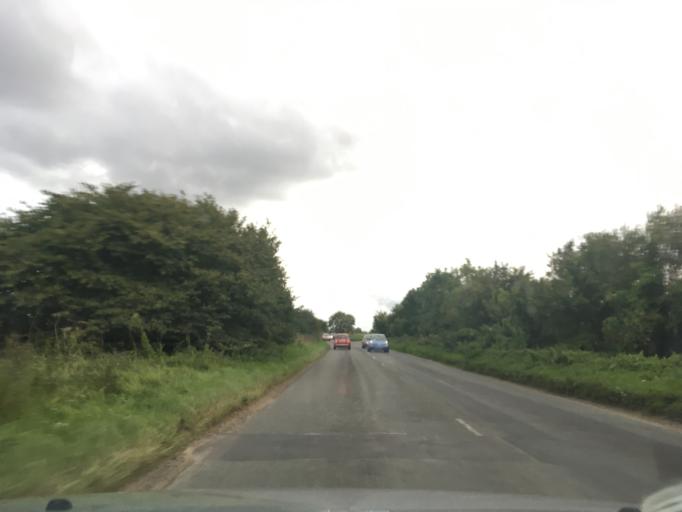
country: GB
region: England
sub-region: Oxfordshire
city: Wheatley
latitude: 51.7826
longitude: -1.1814
